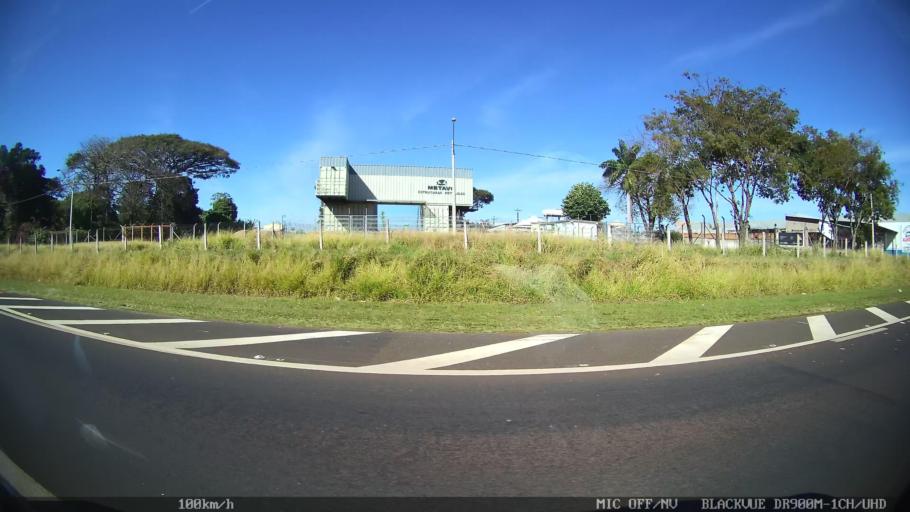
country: BR
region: Sao Paulo
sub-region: Franca
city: Franca
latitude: -20.5713
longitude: -47.3878
